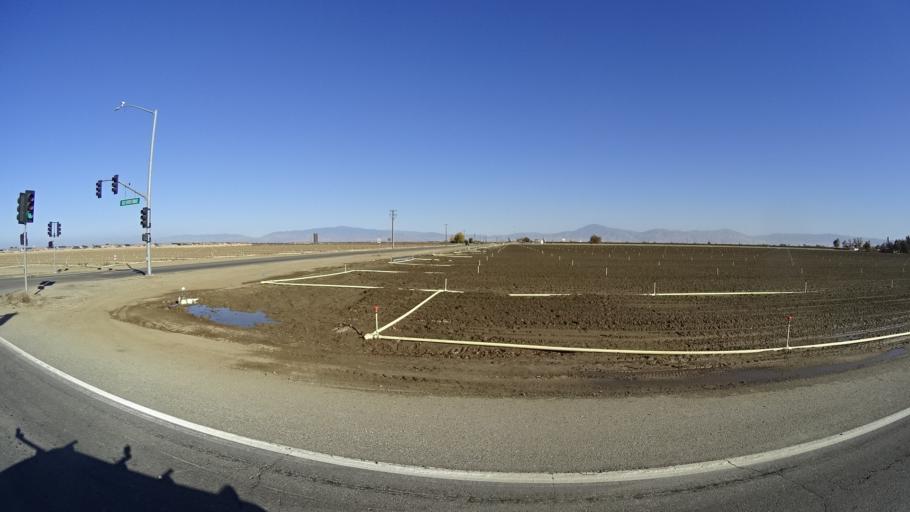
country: US
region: California
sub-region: Kern County
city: Greenacres
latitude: 35.2822
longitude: -119.1105
